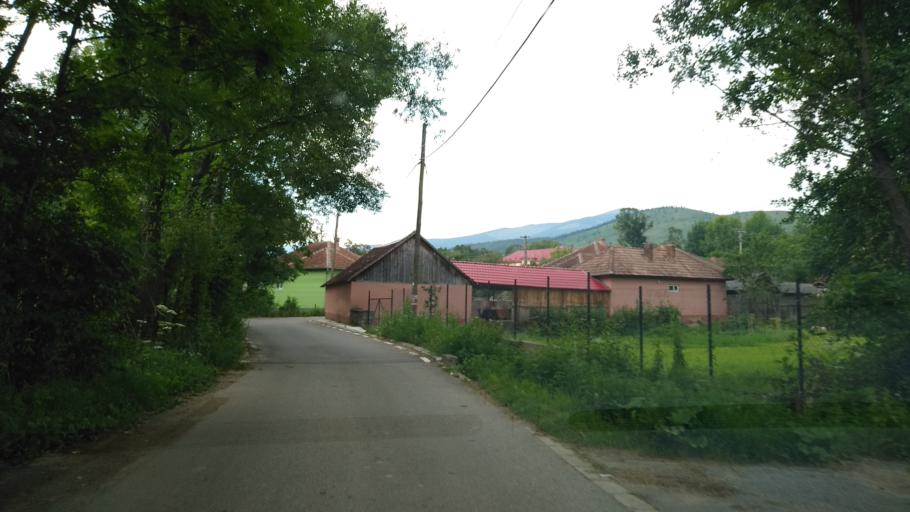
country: RO
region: Hunedoara
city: Salasu de Sus
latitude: 45.4990
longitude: 22.9686
